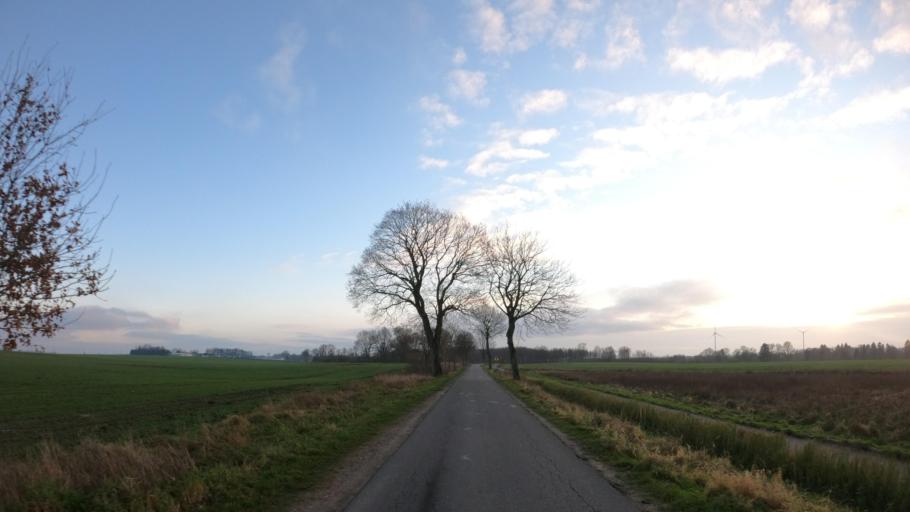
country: PL
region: West Pomeranian Voivodeship
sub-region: Powiat bialogardzki
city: Karlino
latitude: 54.1066
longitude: 15.8871
